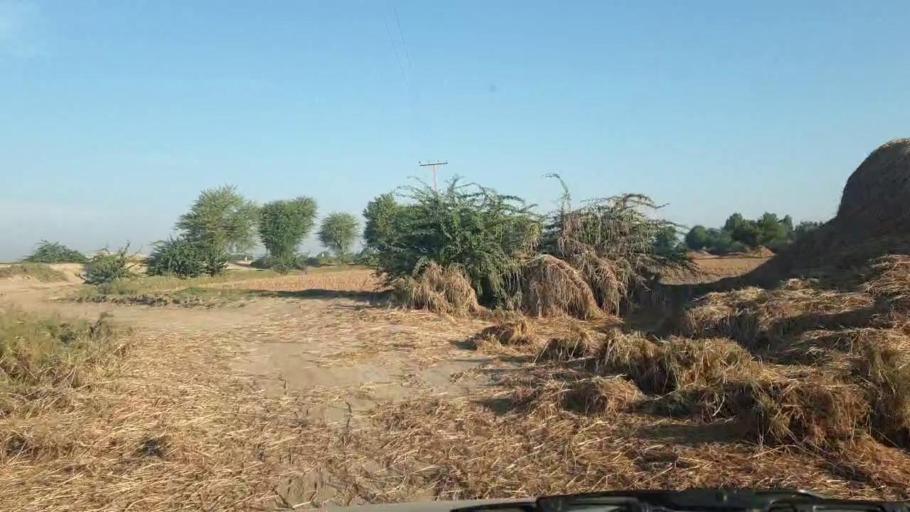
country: PK
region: Sindh
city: Talhar
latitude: 24.7981
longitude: 68.8171
